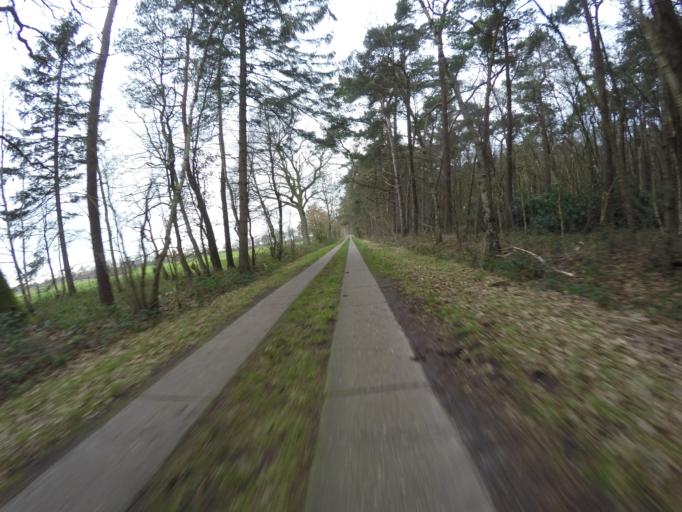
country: DE
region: Schleswig-Holstein
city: Hemdingen
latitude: 53.7830
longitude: 9.8408
